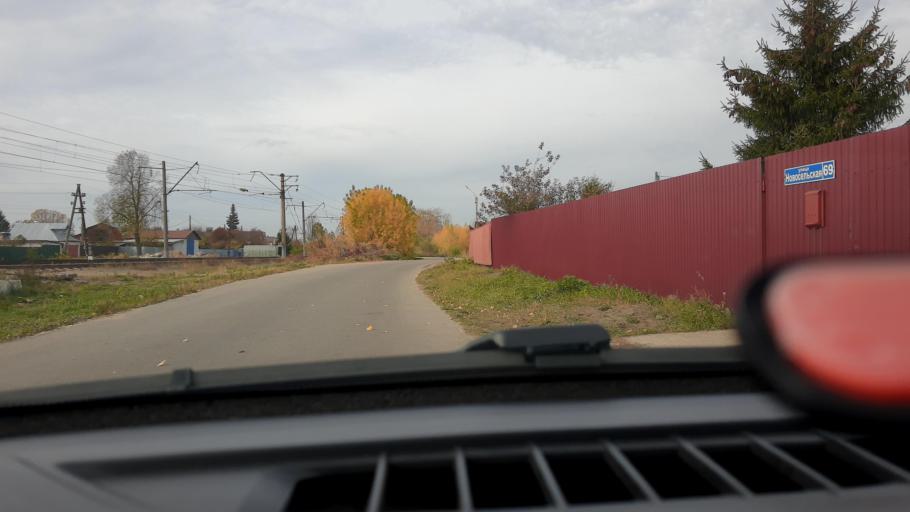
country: RU
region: Nizjnij Novgorod
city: Gorbatovka
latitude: 56.3712
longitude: 43.8235
